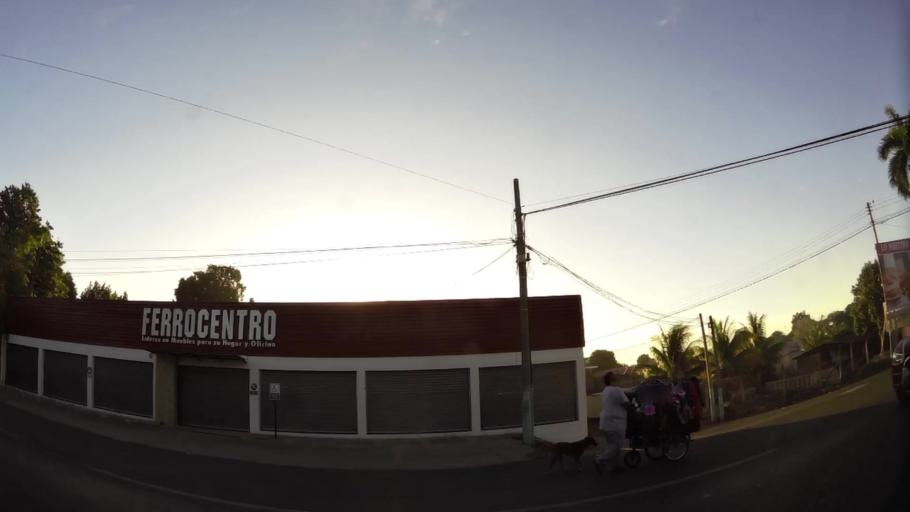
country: SV
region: Sonsonate
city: Sonsonate
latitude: 13.7232
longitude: -89.7187
